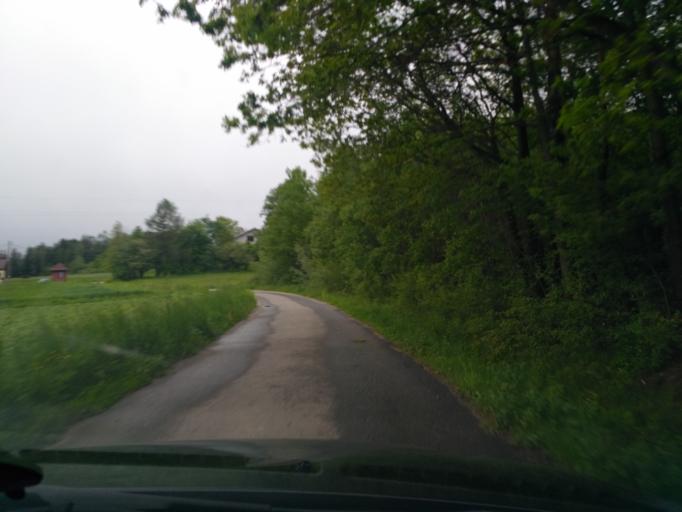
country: PL
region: Subcarpathian Voivodeship
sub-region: Powiat debicki
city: Jodlowa
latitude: 49.8570
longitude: 21.2452
